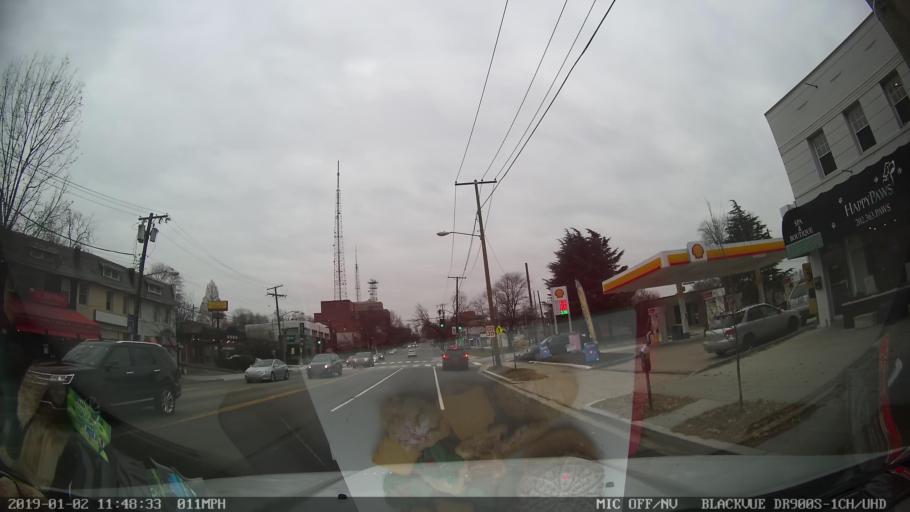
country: US
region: Maryland
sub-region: Montgomery County
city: Friendship Village
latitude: 38.9538
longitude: -77.0823
